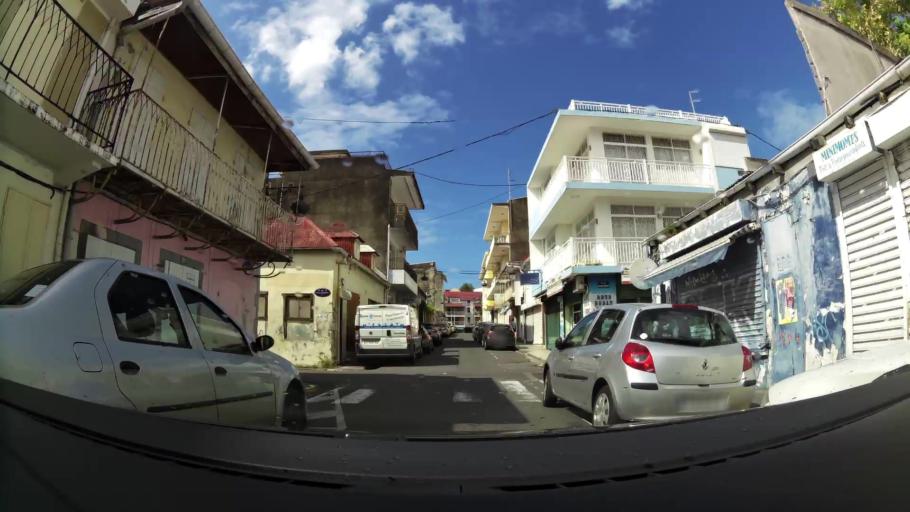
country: GP
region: Guadeloupe
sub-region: Guadeloupe
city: Basse-Terre
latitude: 15.9976
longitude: -61.7320
